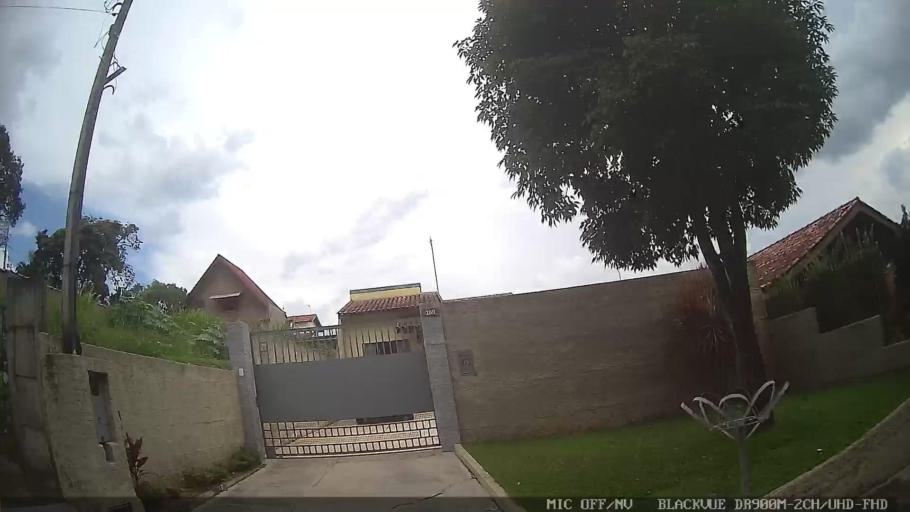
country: BR
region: Sao Paulo
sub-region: Atibaia
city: Atibaia
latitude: -23.1390
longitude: -46.5562
